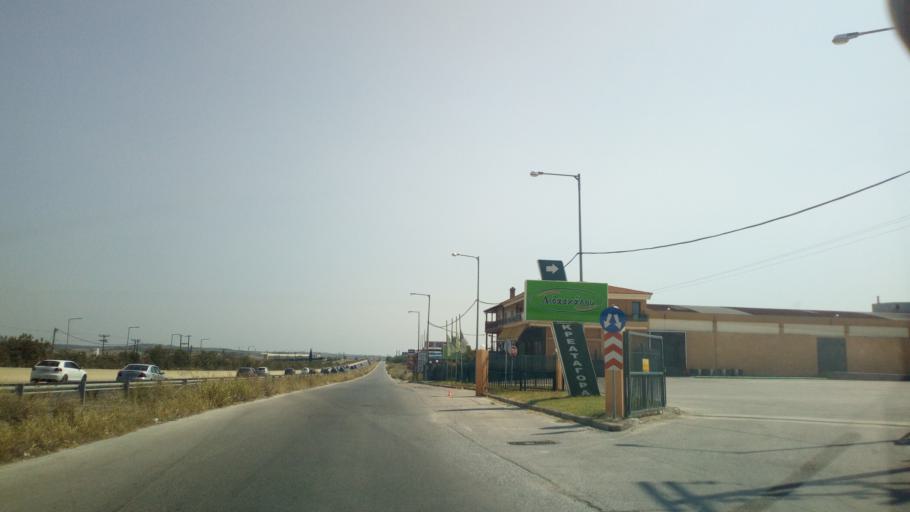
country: GR
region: Central Macedonia
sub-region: Nomos Chalkidikis
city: Lakkoma
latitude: 40.3846
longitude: 23.0382
